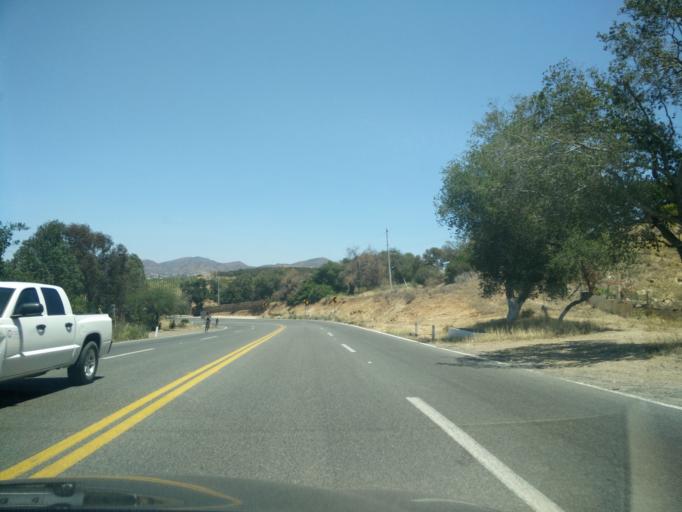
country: MX
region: Baja California
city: El Sauzal
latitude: 31.9636
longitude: -116.6584
